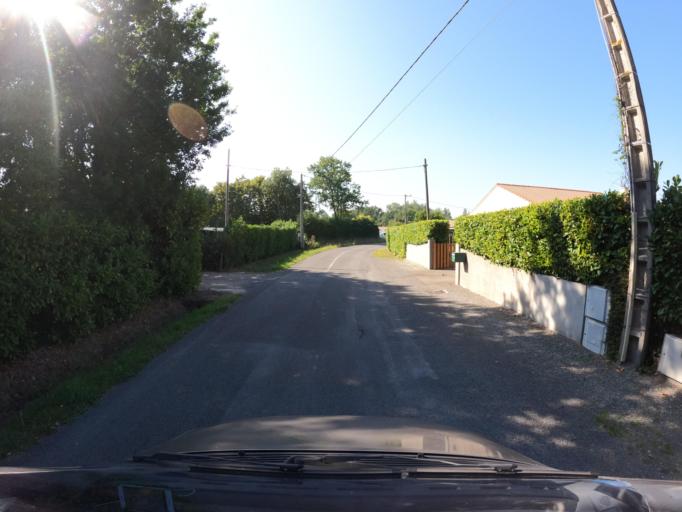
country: FR
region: Pays de la Loire
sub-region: Departement de la Loire-Atlantique
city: Geneston
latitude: 47.0617
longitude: -1.5374
